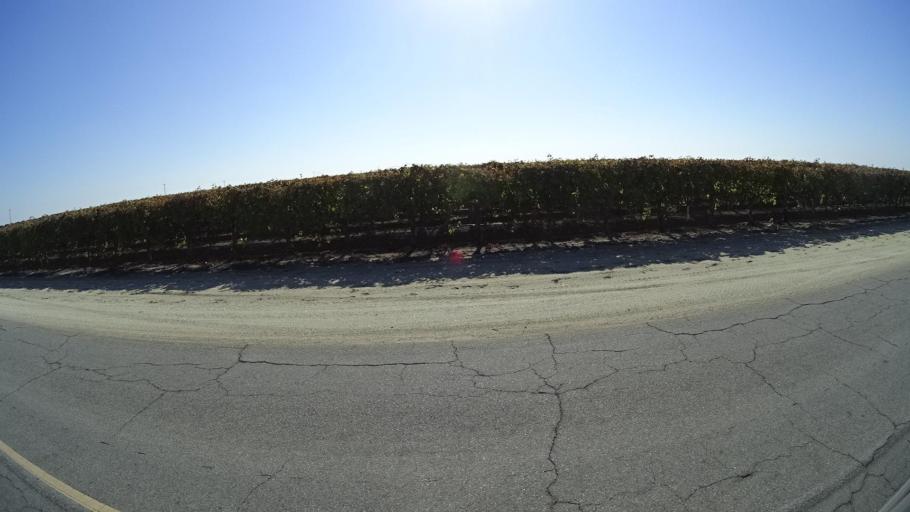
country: US
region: California
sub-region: Kern County
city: McFarland
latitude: 35.7035
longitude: -119.1725
